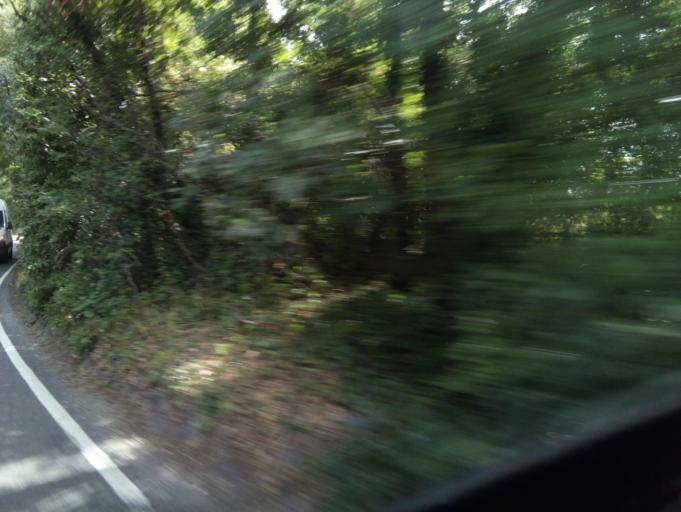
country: GB
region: England
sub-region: Surrey
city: Godstone
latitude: 51.1921
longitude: -0.0666
